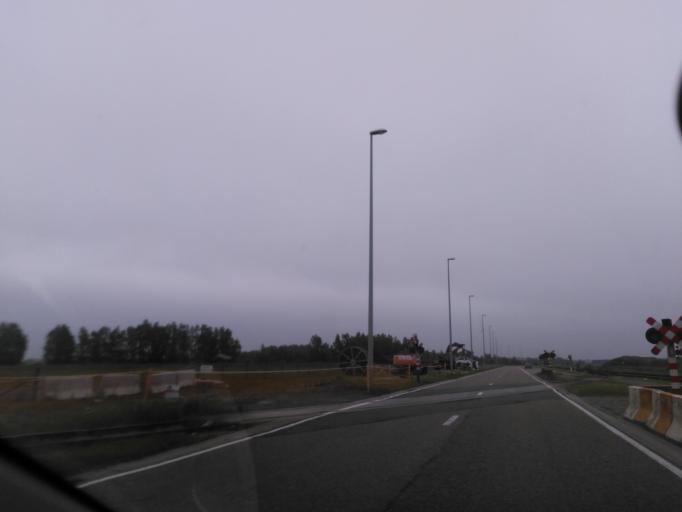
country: BE
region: Flanders
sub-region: Provincie Oost-Vlaanderen
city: Beveren
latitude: 51.2627
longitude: 4.2003
